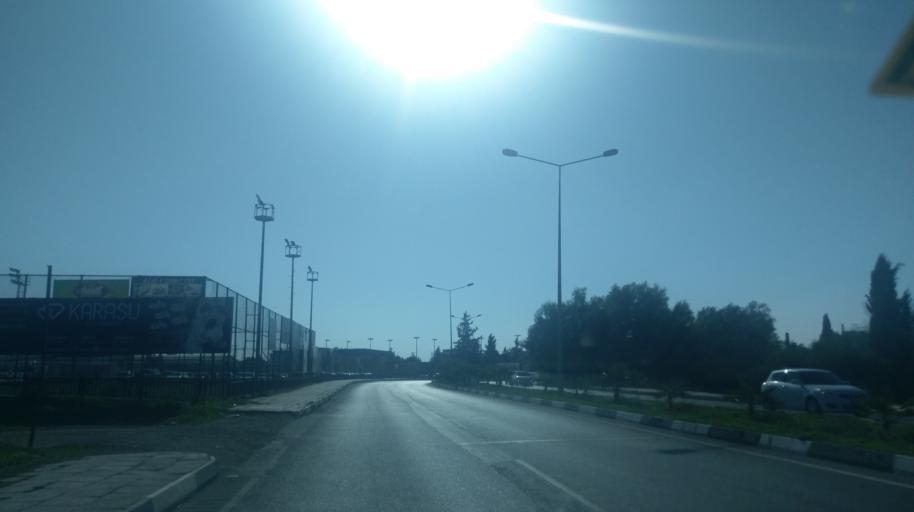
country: CY
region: Lefkosia
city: Nicosia
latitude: 35.2148
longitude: 33.3341
